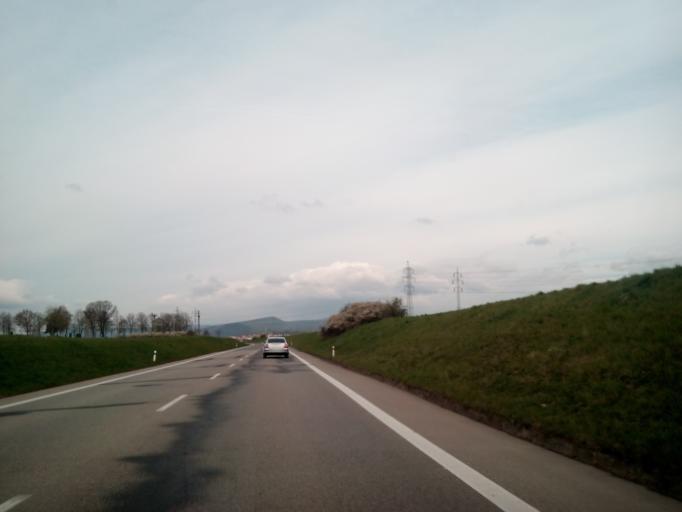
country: SK
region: Kosicky
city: Moldava nad Bodvou
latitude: 48.6021
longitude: 21.0256
